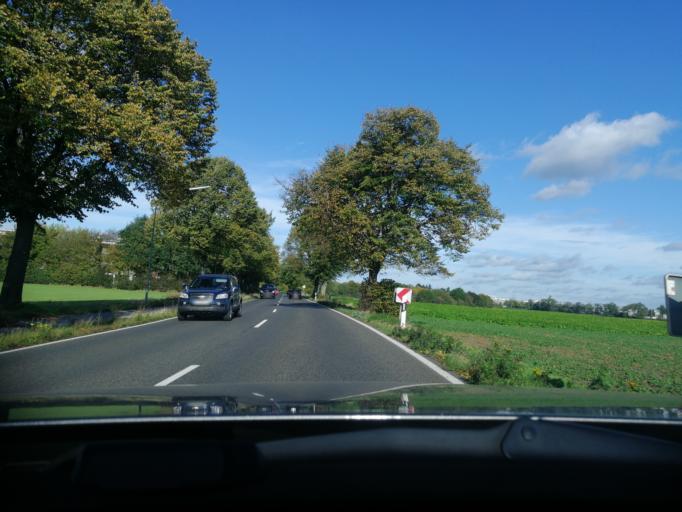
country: DE
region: North Rhine-Westphalia
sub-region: Regierungsbezirk Dusseldorf
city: Neuss
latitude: 51.1484
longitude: 6.7404
